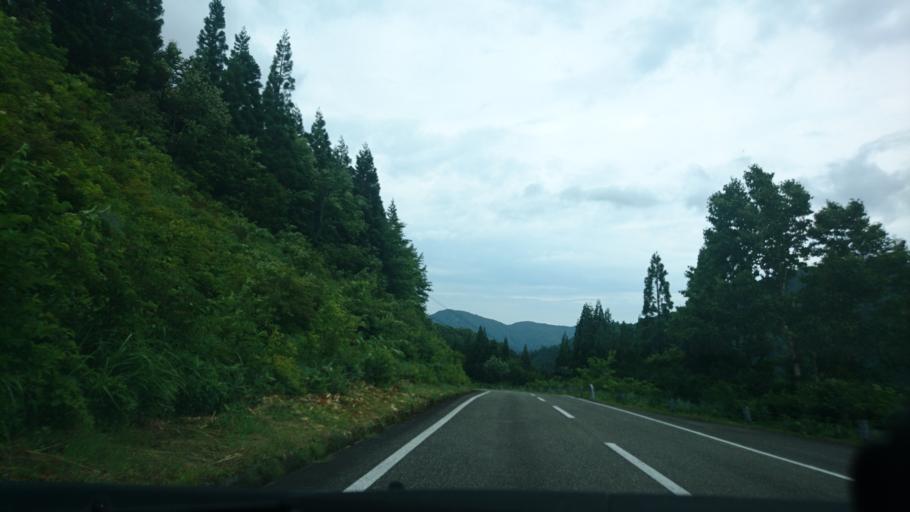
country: JP
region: Akita
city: Yuzawa
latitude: 39.1595
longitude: 140.7487
